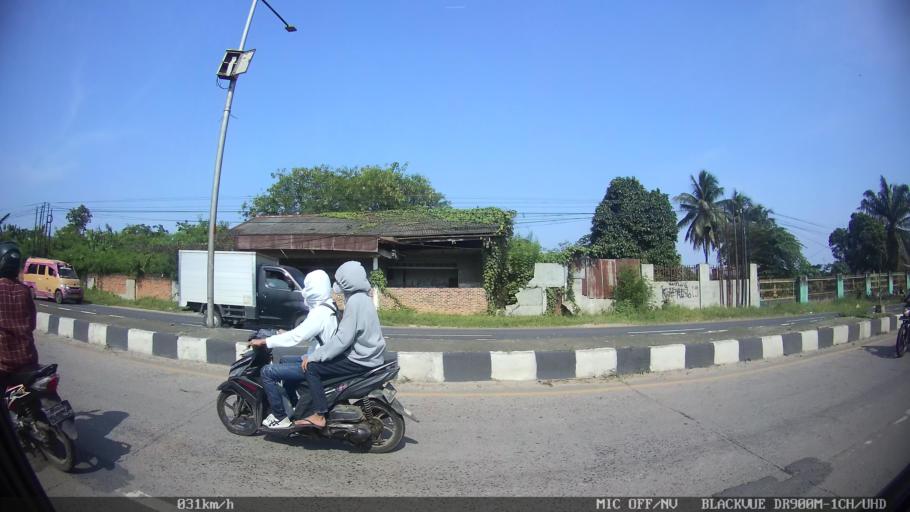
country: ID
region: Lampung
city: Natar
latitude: -5.2361
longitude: 105.1713
